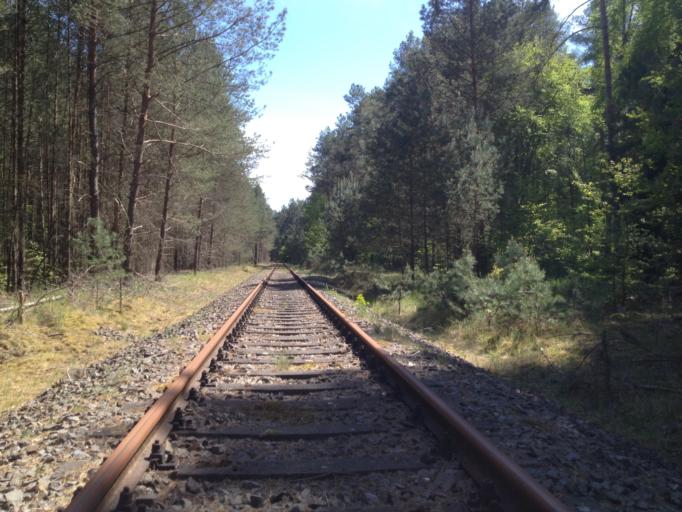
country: DE
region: Brandenburg
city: Lychen
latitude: 53.1757
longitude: 13.3519
